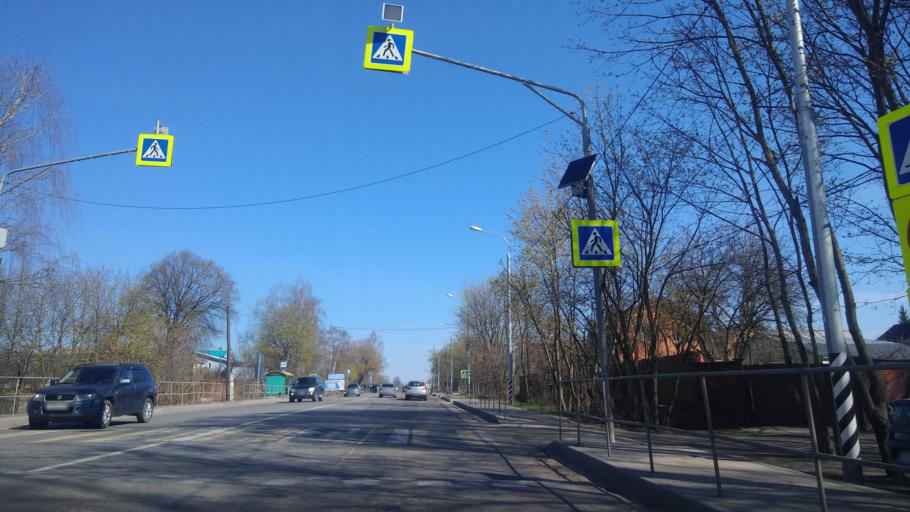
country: RU
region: Moskovskaya
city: Pushkino
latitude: 56.0145
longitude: 37.8720
